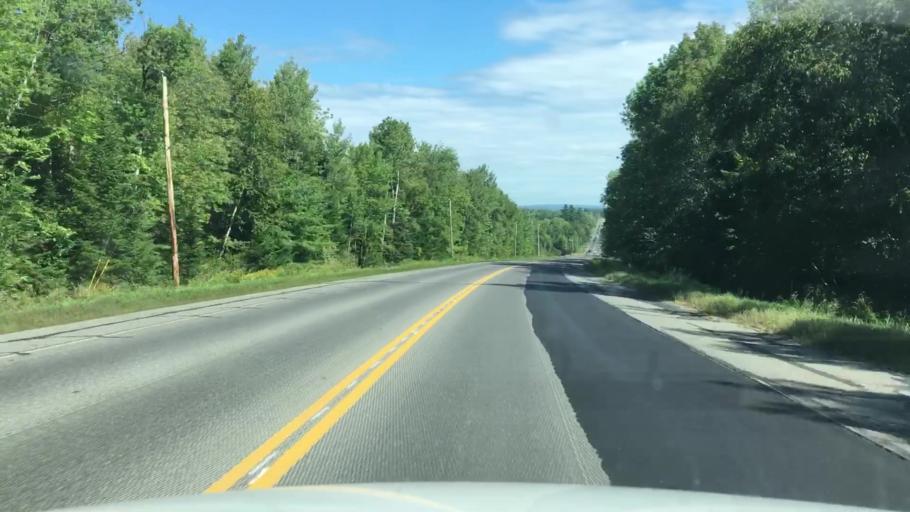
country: US
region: Maine
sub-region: Penobscot County
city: Newport
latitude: 44.8800
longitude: -69.2811
